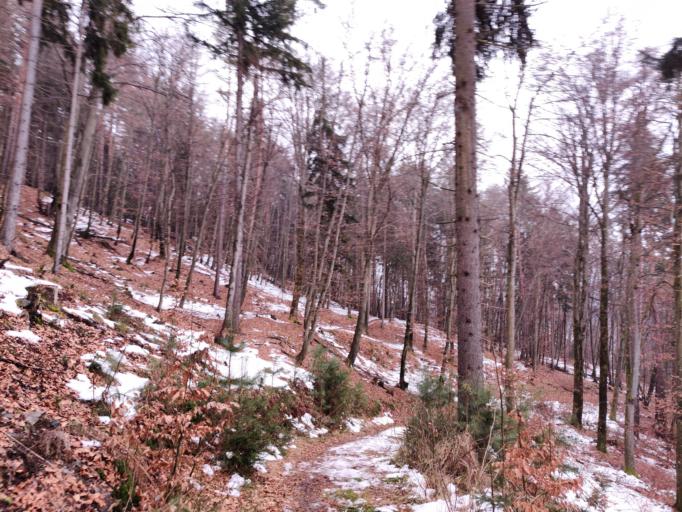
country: AT
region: Carinthia
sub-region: Klagenfurt am Woerthersee
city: Klagenfurt am Woerthersee
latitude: 46.6281
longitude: 14.2643
